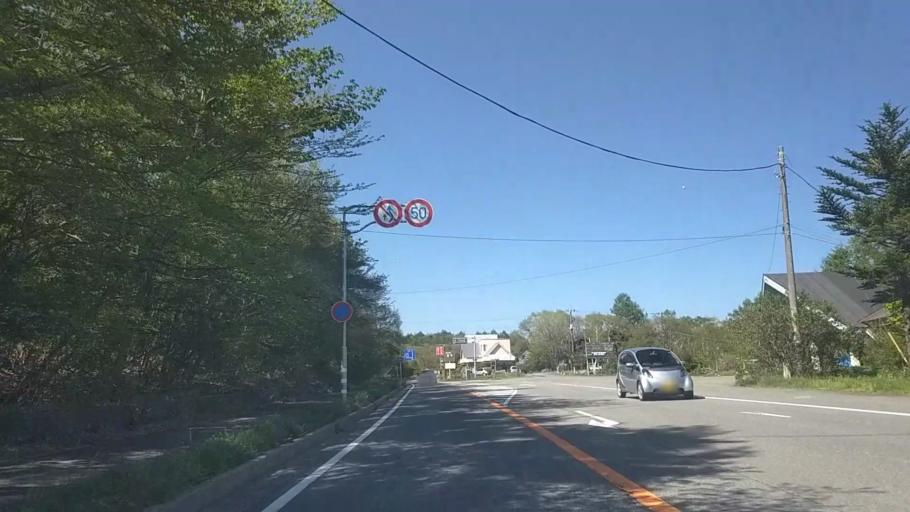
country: JP
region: Yamanashi
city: Nirasaki
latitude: 35.9280
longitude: 138.4423
